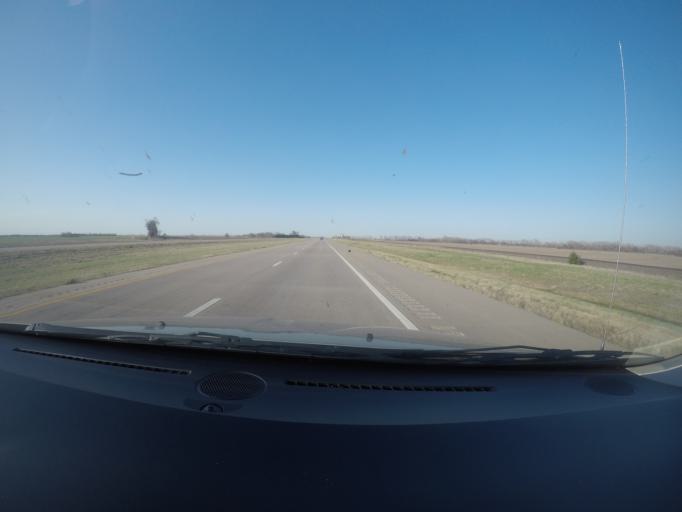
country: US
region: Kansas
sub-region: McPherson County
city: Inman
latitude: 38.2689
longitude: -97.7499
